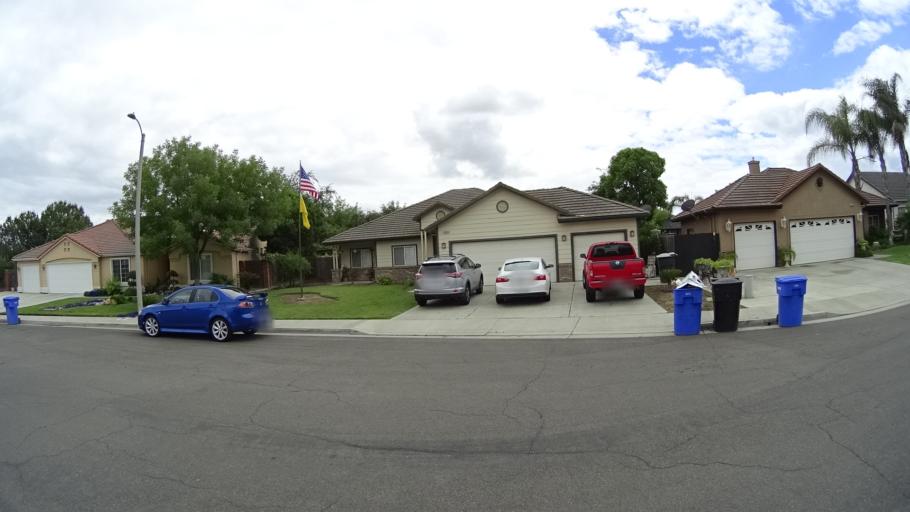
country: US
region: California
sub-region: Kings County
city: Armona
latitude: 36.3319
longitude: -119.6794
